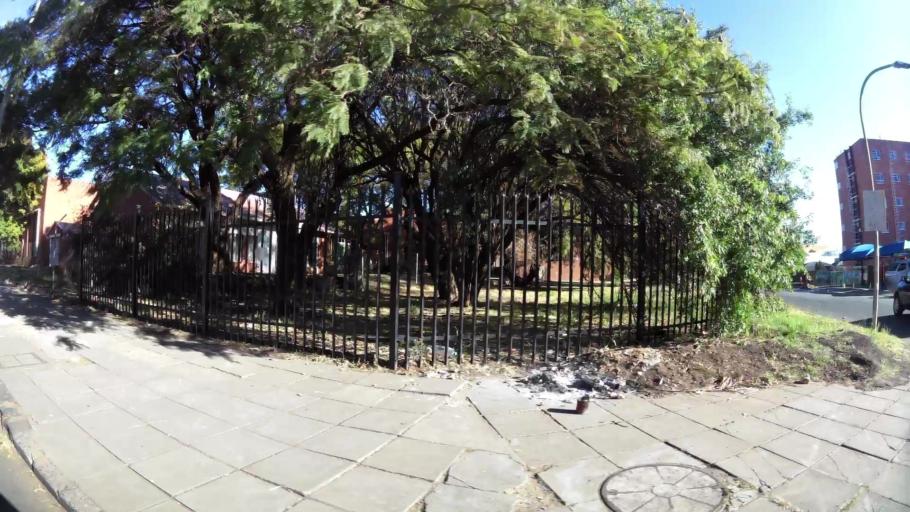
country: ZA
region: Northern Cape
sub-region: Frances Baard District Municipality
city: Kimberley
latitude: -28.7452
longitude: 24.7709
